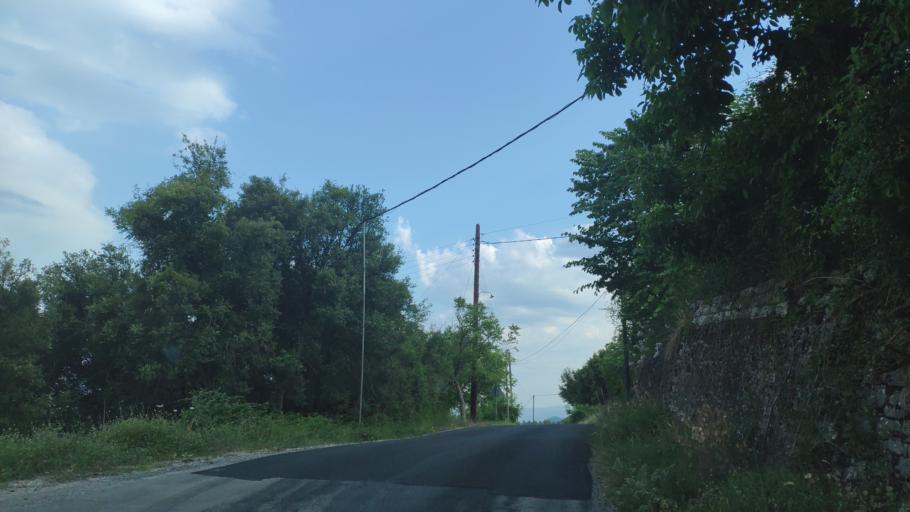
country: GR
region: Epirus
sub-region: Nomos Artas
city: Agios Dimitrios
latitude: 39.3734
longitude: 21.0249
